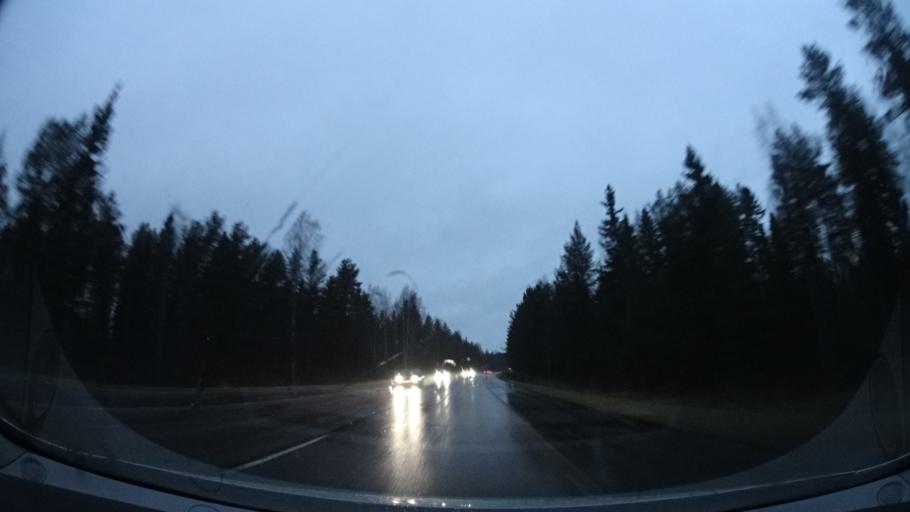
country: SE
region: Vaesterbotten
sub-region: Skelleftea Kommun
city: Skelleftea
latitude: 64.7570
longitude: 21.0106
